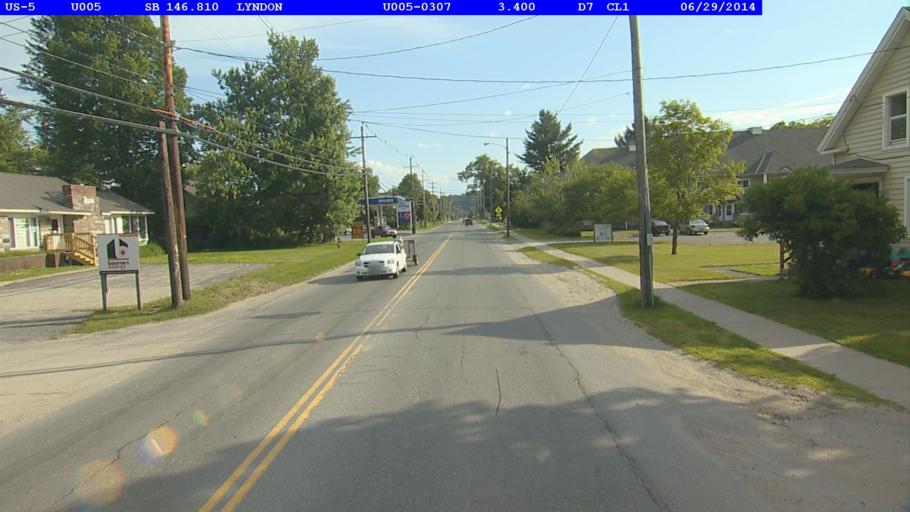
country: US
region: Vermont
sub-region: Caledonia County
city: Lyndonville
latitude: 44.5406
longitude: -72.0017
